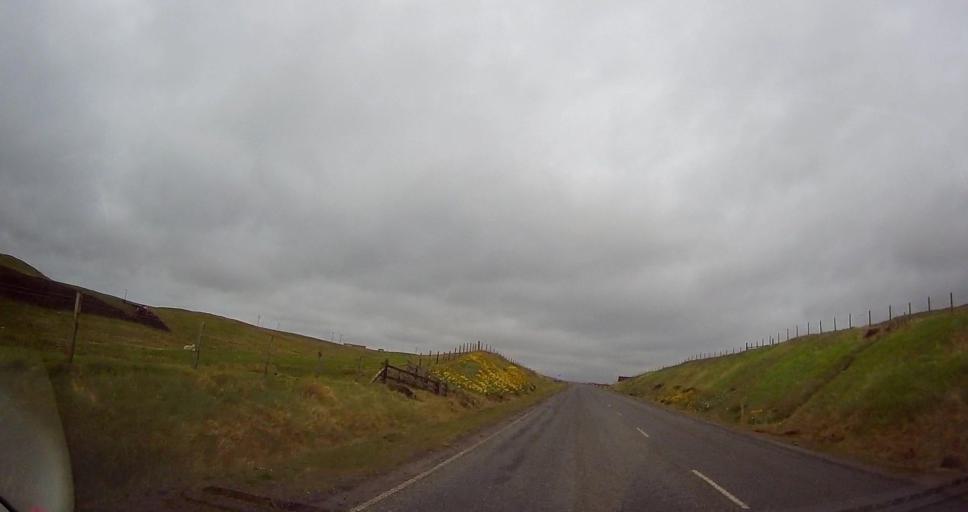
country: GB
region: Scotland
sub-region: Shetland Islands
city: Lerwick
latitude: 60.3750
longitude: -1.3379
